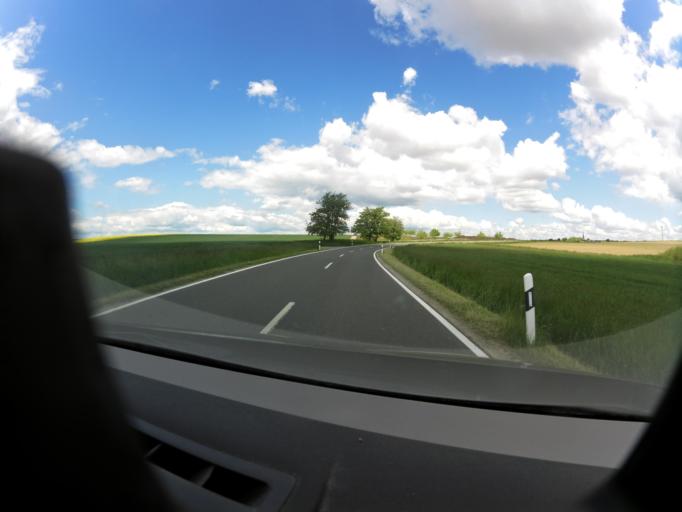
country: DE
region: Bavaria
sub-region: Regierungsbezirk Unterfranken
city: Prosselsheim
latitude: 49.8849
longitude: 10.1200
